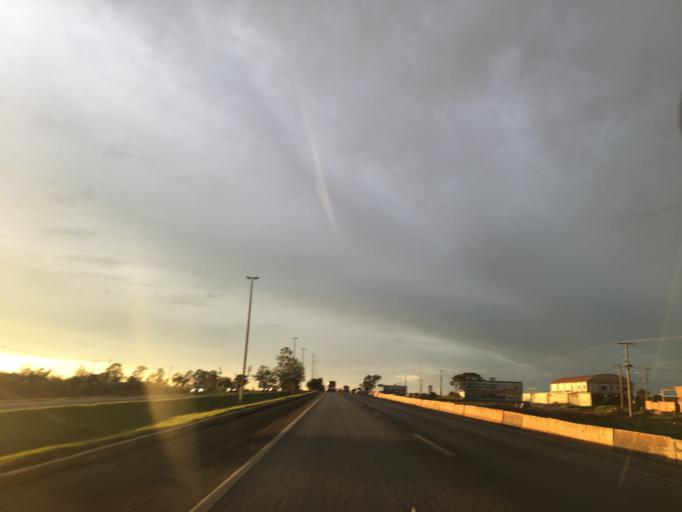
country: BR
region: Federal District
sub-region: Brasilia
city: Brasilia
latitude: -16.0119
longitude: -47.9824
